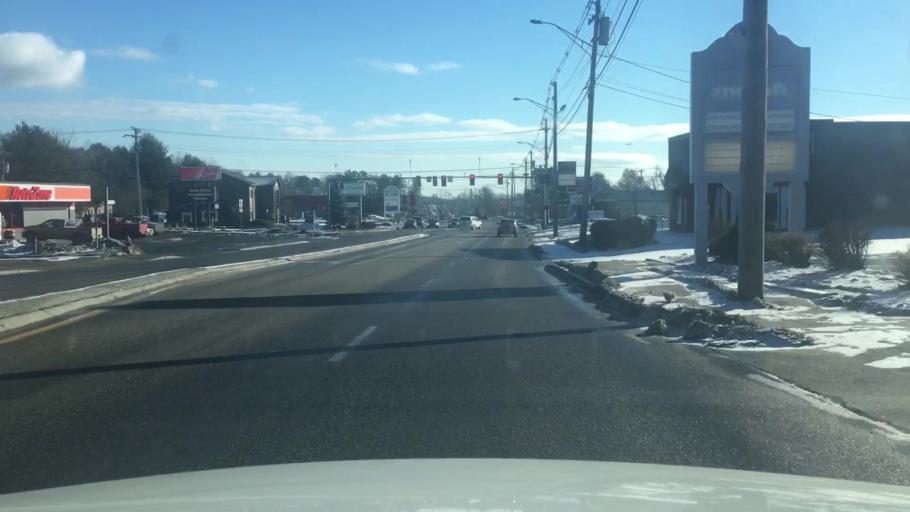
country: US
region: Maine
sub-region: Kennebec County
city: Augusta
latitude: 44.3148
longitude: -69.8030
